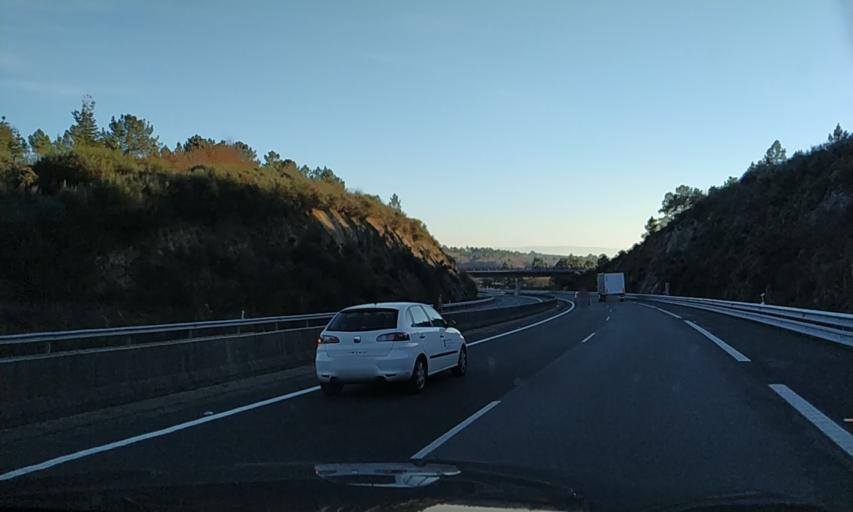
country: ES
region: Galicia
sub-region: Provincia de Ourense
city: Pinor
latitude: 42.5004
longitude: -8.0285
